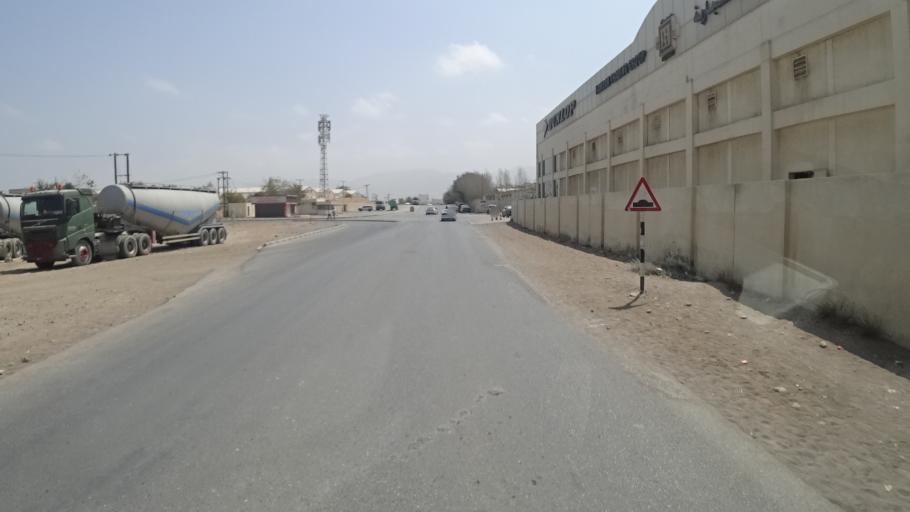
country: OM
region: Muhafazat Masqat
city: Bawshar
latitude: 23.5761
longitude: 58.3549
